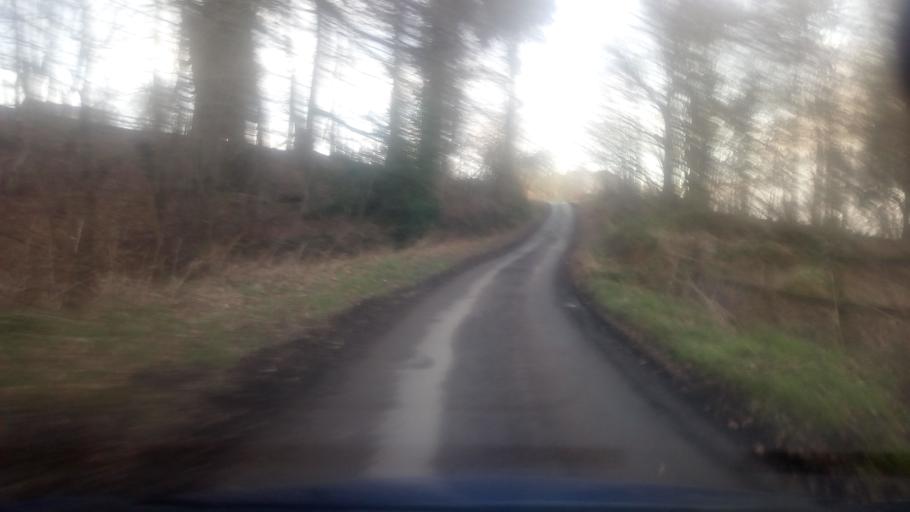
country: GB
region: Scotland
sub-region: The Scottish Borders
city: Jedburgh
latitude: 55.4945
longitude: -2.5572
